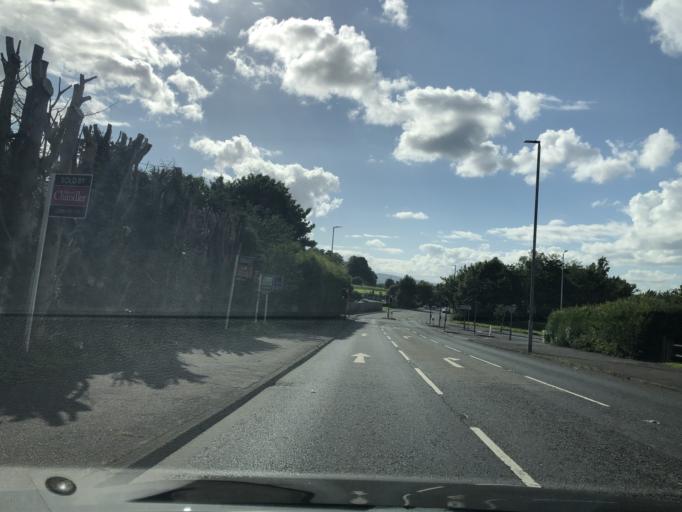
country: GB
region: Northern Ireland
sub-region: Castlereagh District
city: Dundonald
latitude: 54.5873
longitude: -5.8135
